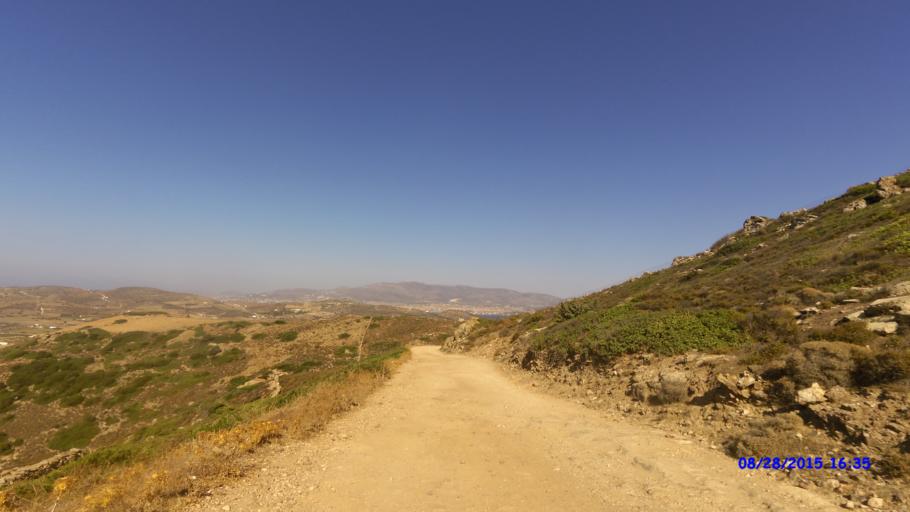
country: GR
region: South Aegean
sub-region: Nomos Kykladon
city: Antiparos
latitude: 37.0068
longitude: 25.0426
